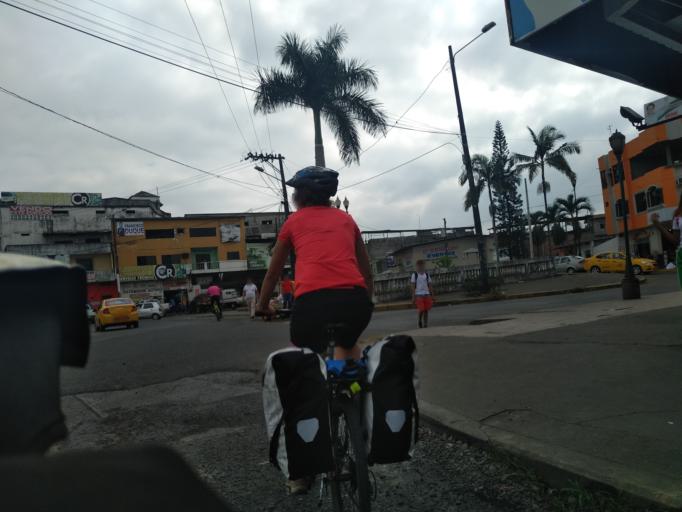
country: EC
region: Los Rios
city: Quevedo
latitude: -1.0314
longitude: -79.4710
